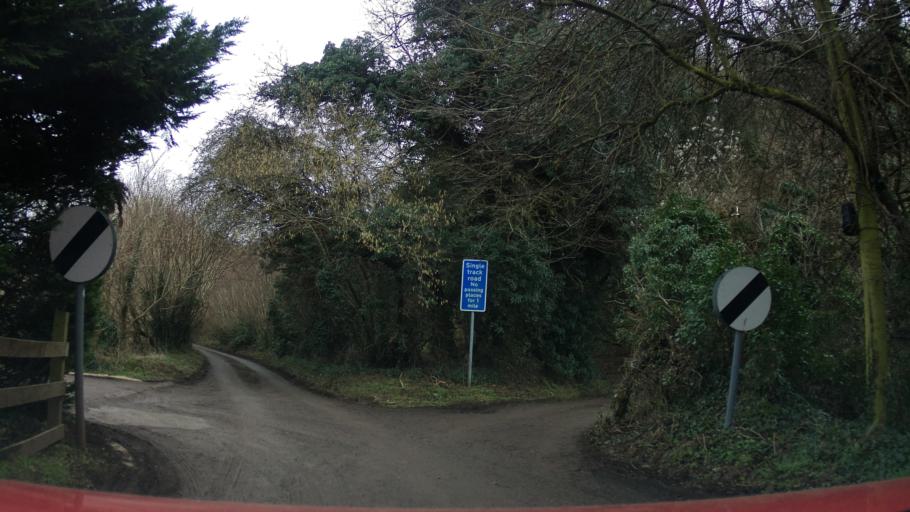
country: GB
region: England
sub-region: Wiltshire
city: Biddestone
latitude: 51.4715
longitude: -2.2301
